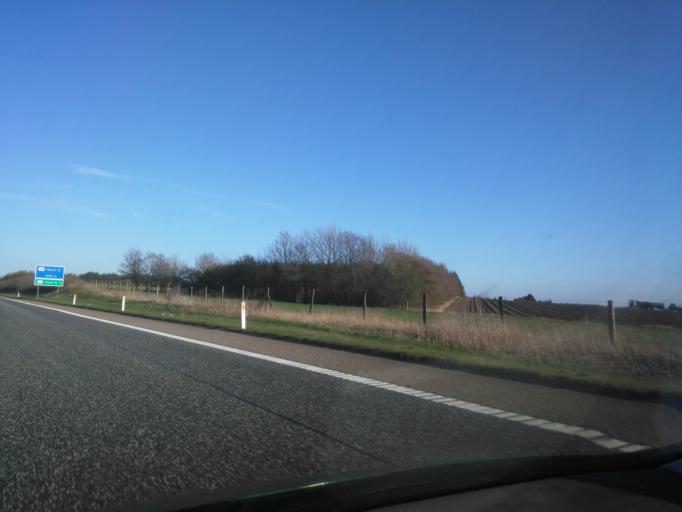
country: DK
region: Central Jutland
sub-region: Ikast-Brande Kommune
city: Ikast
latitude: 56.1186
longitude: 9.1165
